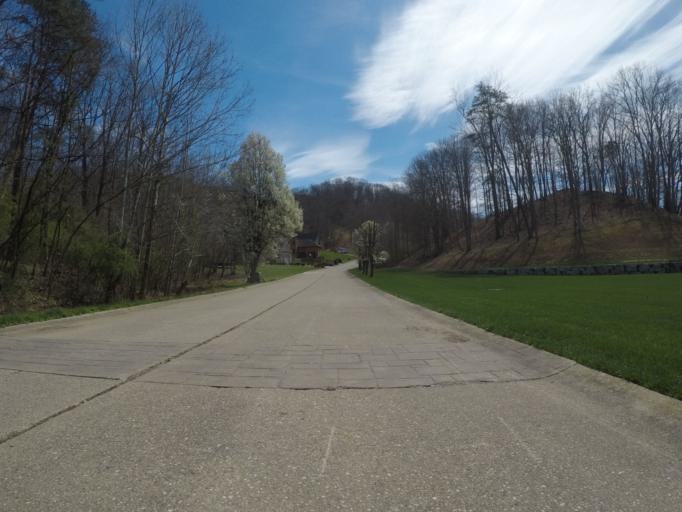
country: US
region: West Virginia
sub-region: Cabell County
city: Pea Ridge
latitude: 38.4055
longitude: -82.3133
